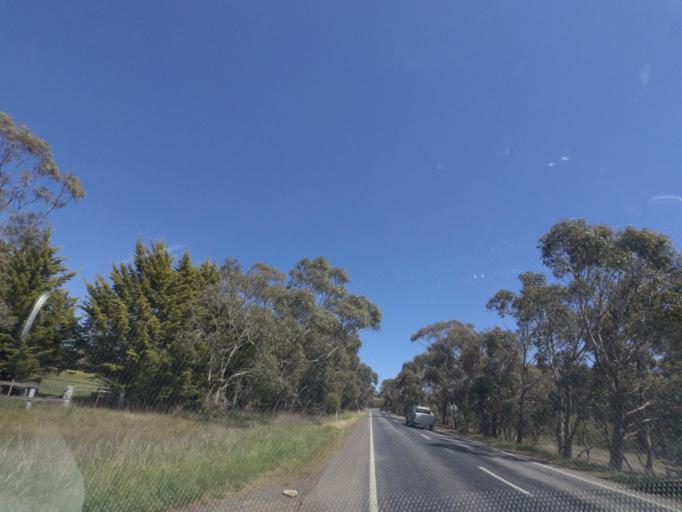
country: AU
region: Victoria
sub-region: Hume
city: Sunbury
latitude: -37.2989
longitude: 144.8204
